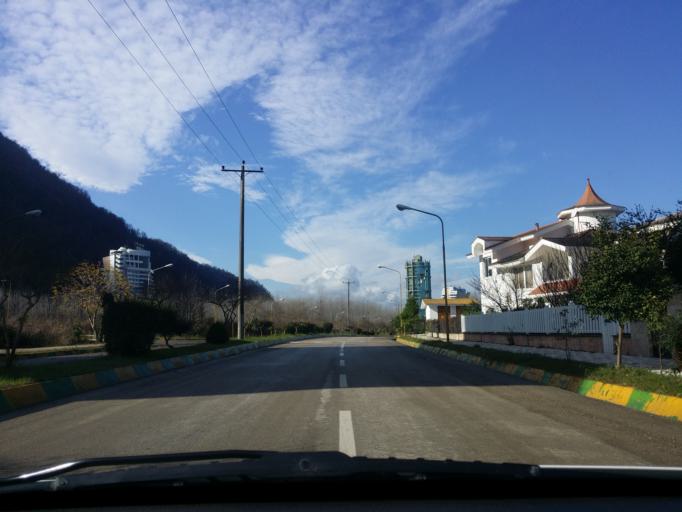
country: IR
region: Mazandaran
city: Chalus
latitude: 36.6670
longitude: 51.3111
